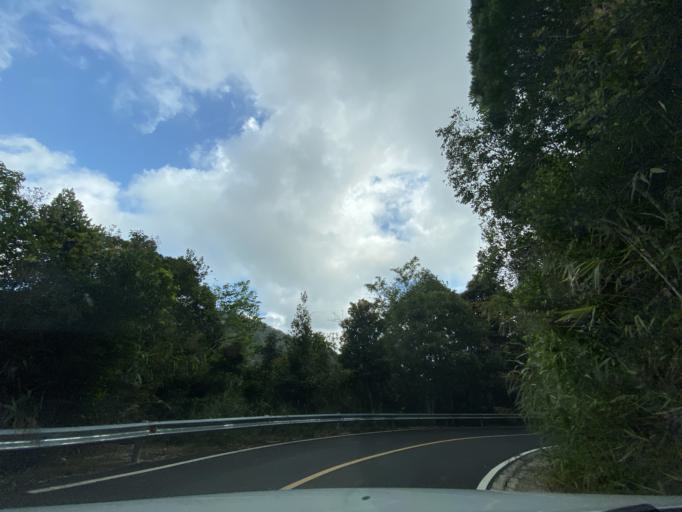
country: CN
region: Hainan
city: Diaoluoshan
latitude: 18.7031
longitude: 109.8825
